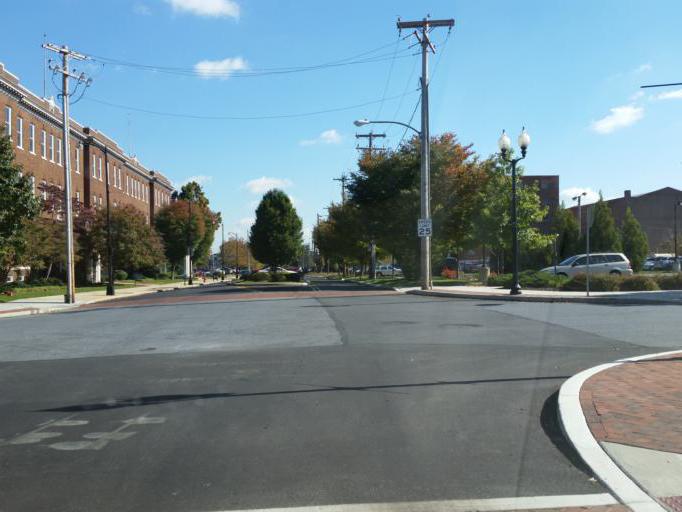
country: US
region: Pennsylvania
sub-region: Lancaster County
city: Lancaster
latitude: 40.0514
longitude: -76.3152
